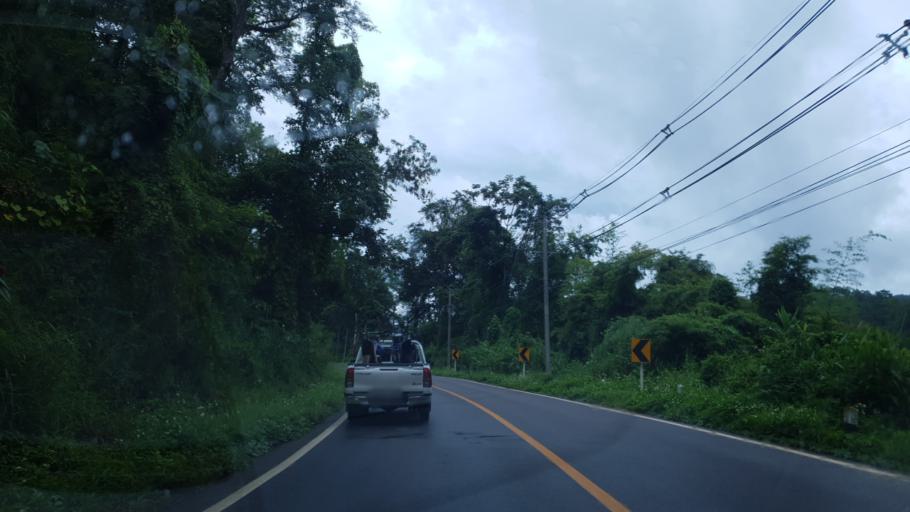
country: TH
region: Mae Hong Son
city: Ban Huai I Huak
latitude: 18.1460
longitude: 98.0232
